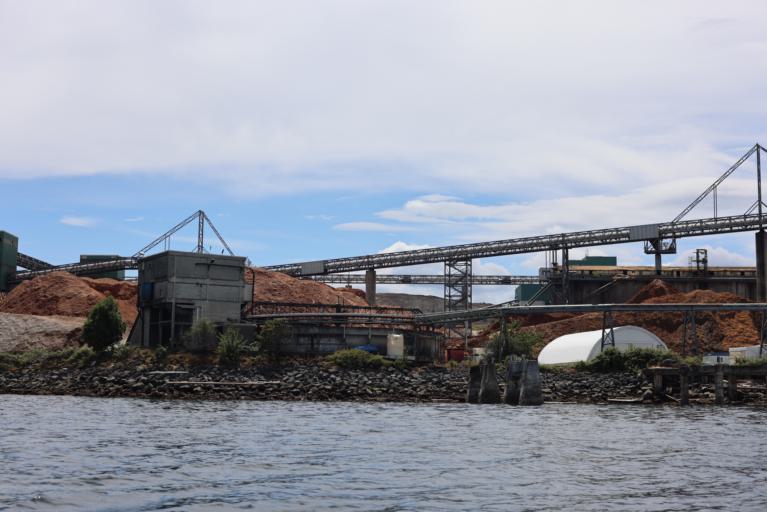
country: CA
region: British Columbia
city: Nanaimo
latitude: 49.1404
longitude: -123.8545
